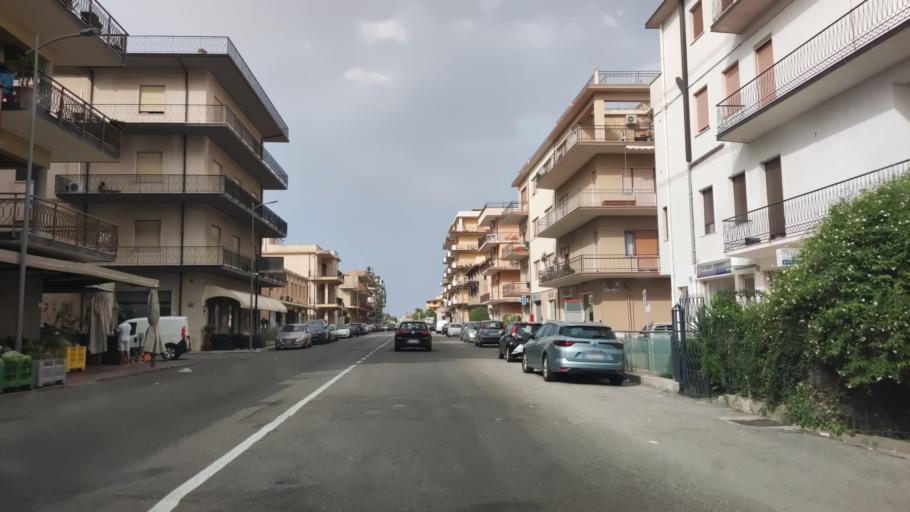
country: IT
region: Calabria
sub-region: Provincia di Reggio Calabria
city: Locri
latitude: 38.2398
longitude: 16.2699
